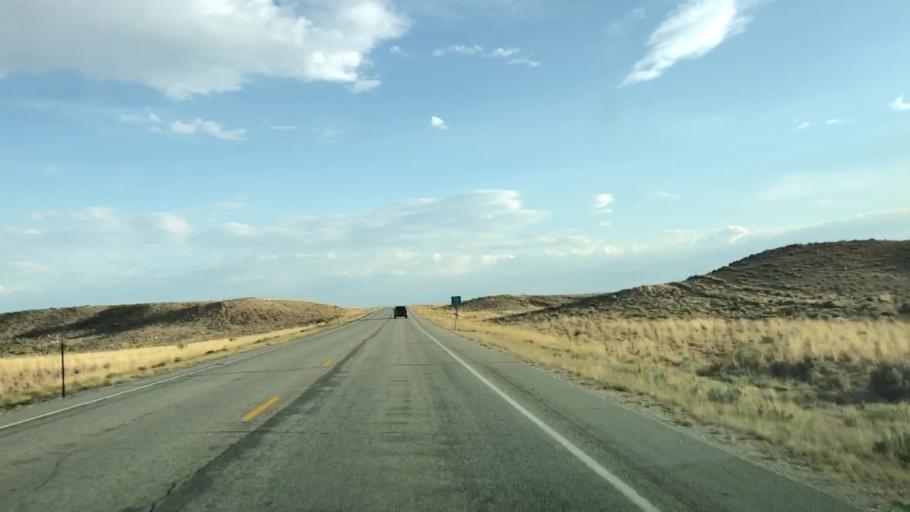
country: US
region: Wyoming
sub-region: Sublette County
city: Pinedale
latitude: 42.3468
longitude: -109.5220
